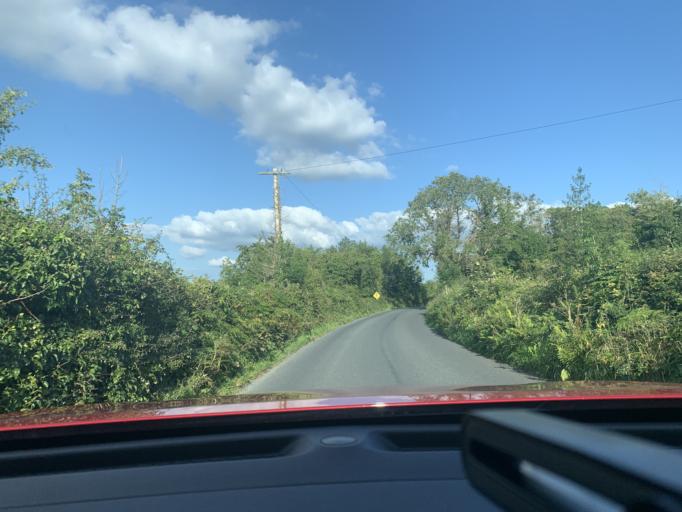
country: IE
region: Connaught
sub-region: Sligo
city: Strandhill
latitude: 54.2009
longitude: -8.5844
